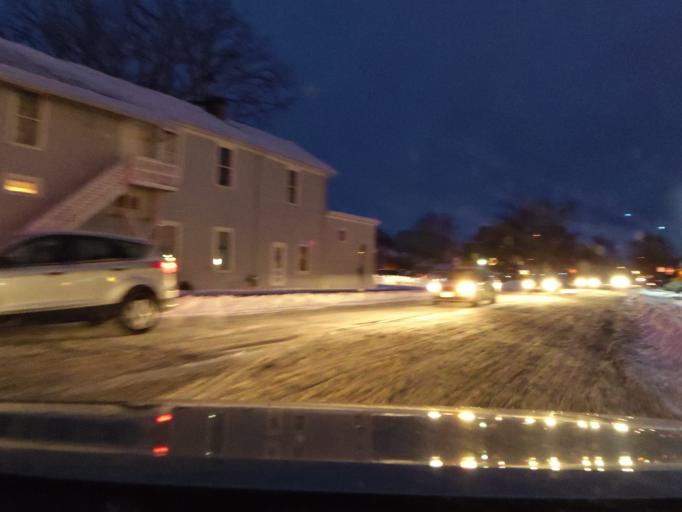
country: US
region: Wisconsin
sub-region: Dunn County
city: Menomonie
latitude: 44.8764
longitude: -91.9234
